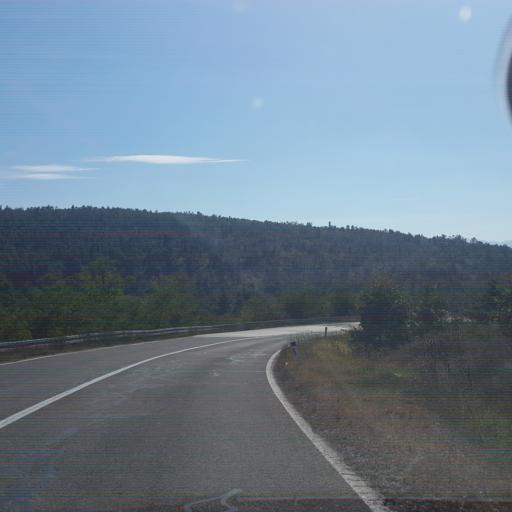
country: RS
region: Central Serbia
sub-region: Zajecarski Okrug
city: Knjazevac
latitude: 43.4721
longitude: 22.2274
